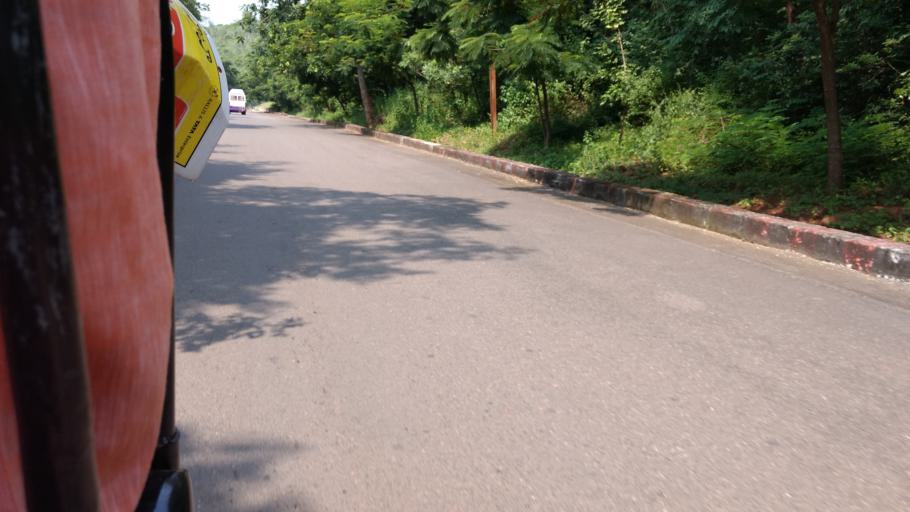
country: IN
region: Andhra Pradesh
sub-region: East Godavari
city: Tuni
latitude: 17.2795
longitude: 82.3993
